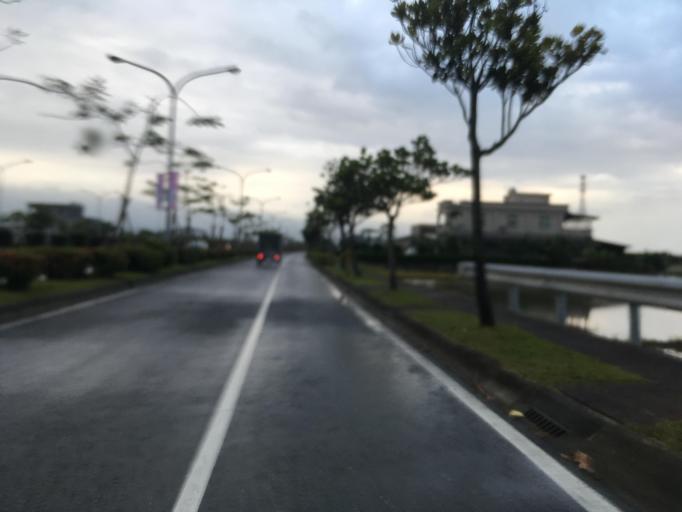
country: TW
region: Taiwan
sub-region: Yilan
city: Yilan
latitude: 24.7268
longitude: 121.7723
